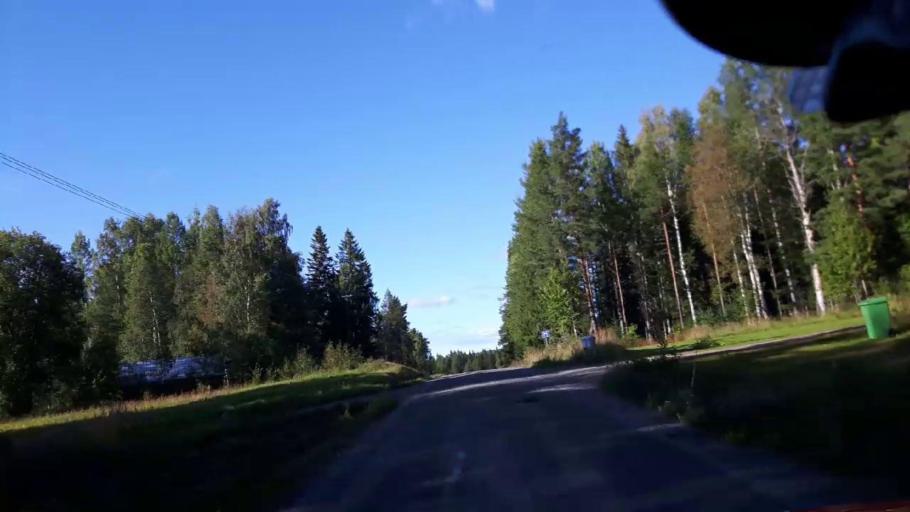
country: SE
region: Jaemtland
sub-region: Ragunda Kommun
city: Hammarstrand
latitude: 63.5207
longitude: 16.0562
